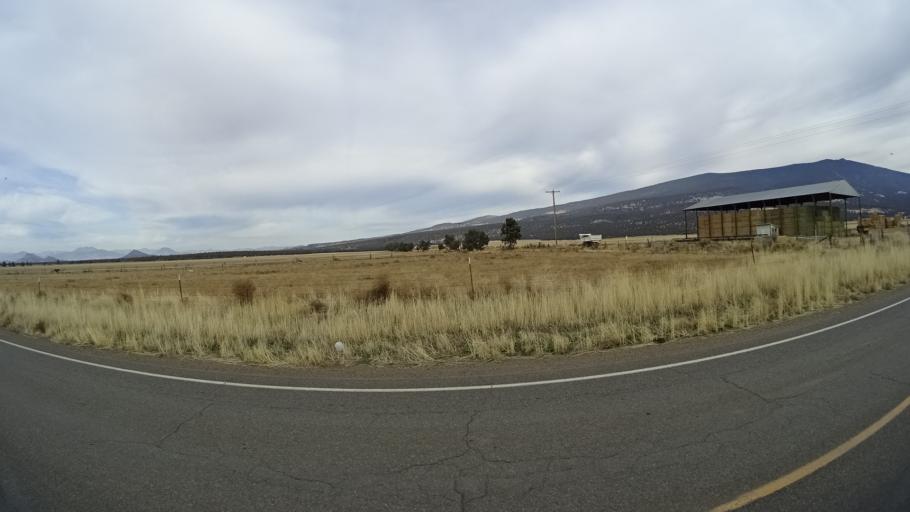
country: US
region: California
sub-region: Siskiyou County
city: Weed
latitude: 41.5943
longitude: -122.3221
